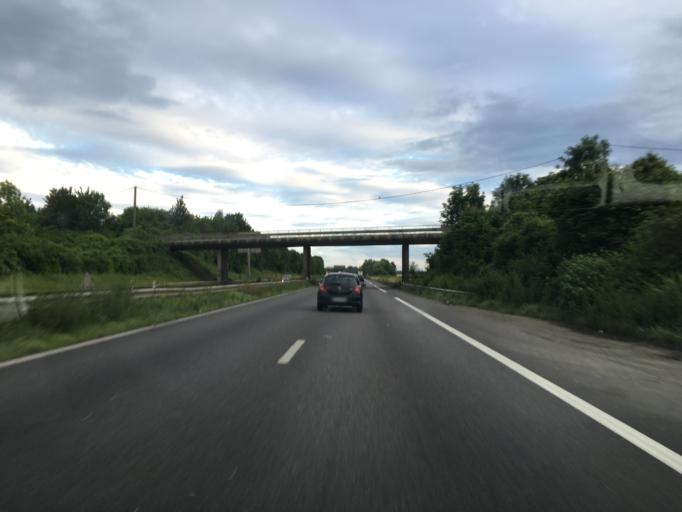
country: FR
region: Ile-de-France
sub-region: Departement de Seine-et-Marne
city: Servon
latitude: 48.6944
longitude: 2.5947
